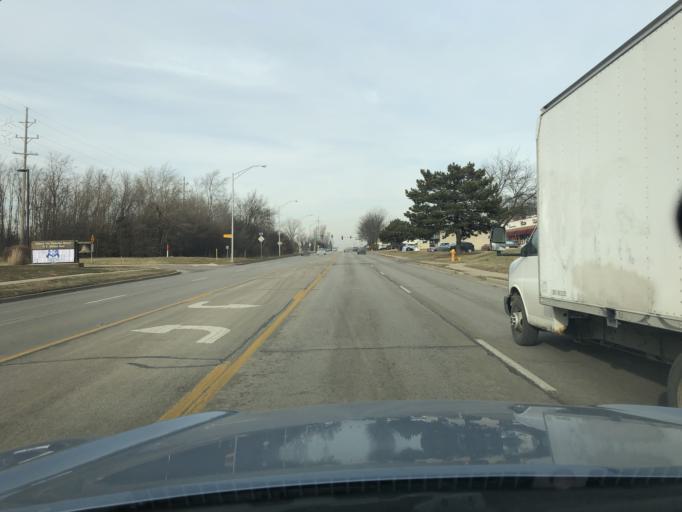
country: US
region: Illinois
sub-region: DuPage County
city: Addison
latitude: 41.9266
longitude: -87.9887
